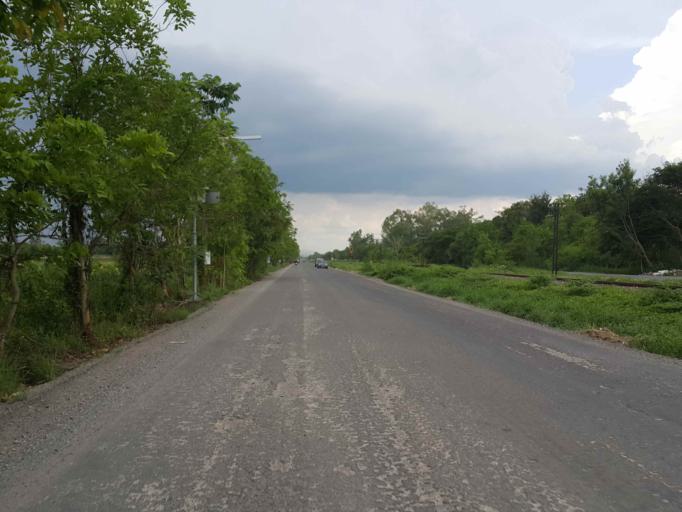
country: TH
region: Chiang Mai
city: Saraphi
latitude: 18.7286
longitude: 99.0340
